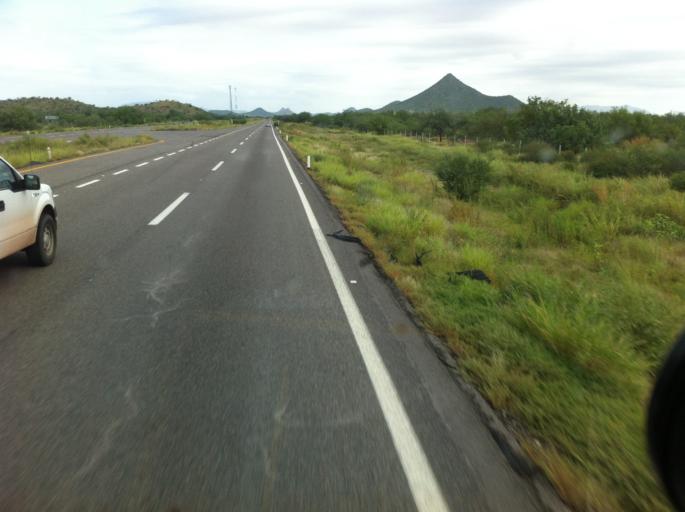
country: MX
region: Sonora
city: Hermosillo
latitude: 28.7880
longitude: -110.9621
